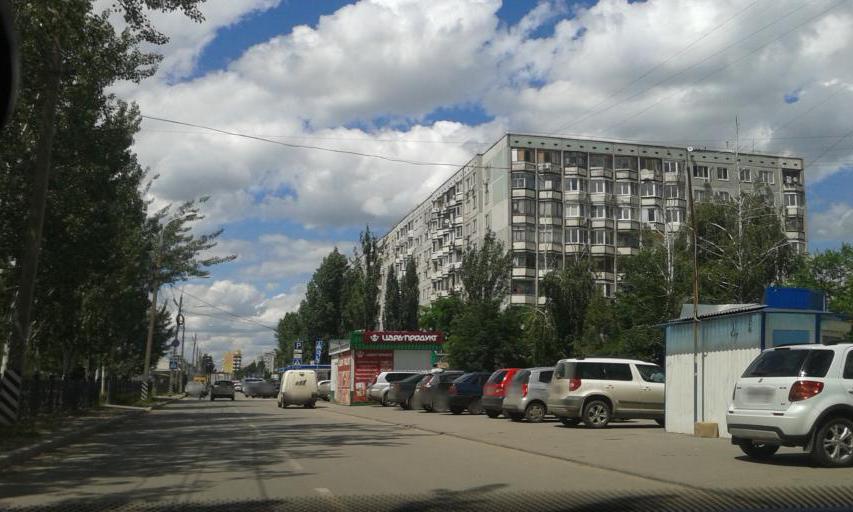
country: RU
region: Volgograd
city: Volgograd
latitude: 48.7558
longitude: 44.5026
